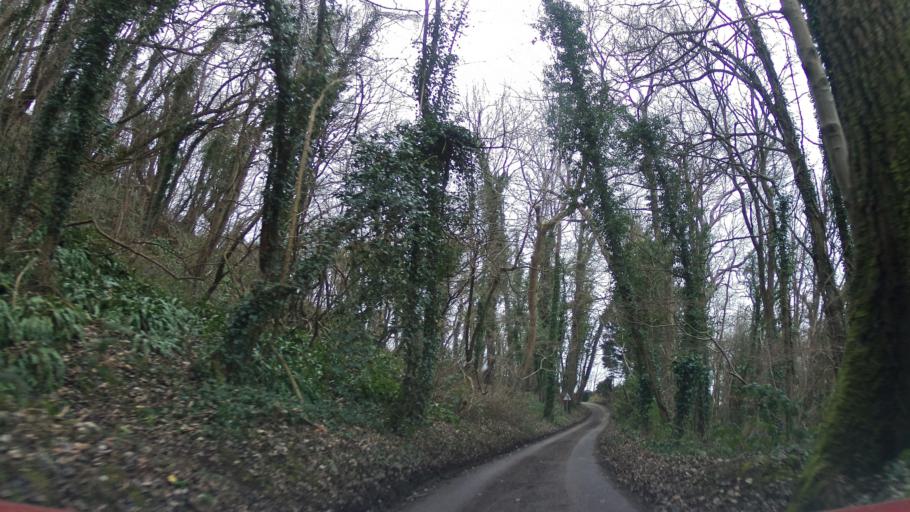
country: GB
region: England
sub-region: Wiltshire
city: Biddestone
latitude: 51.4609
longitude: -2.2263
